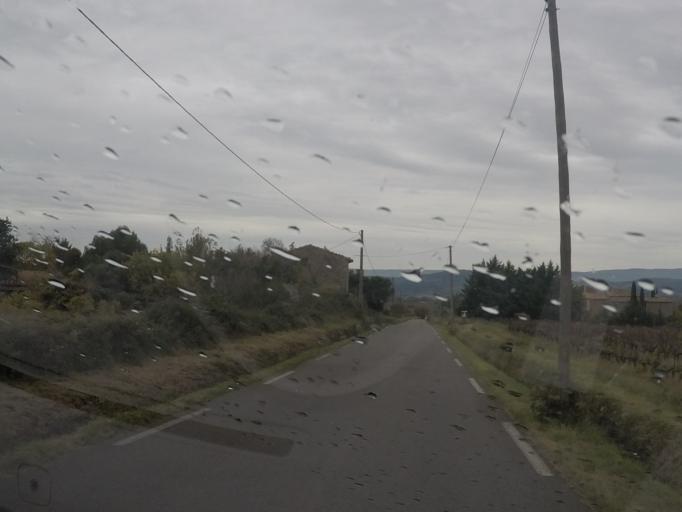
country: FR
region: Provence-Alpes-Cote d'Azur
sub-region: Departement du Vaucluse
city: Bonnieux
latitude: 43.8352
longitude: 5.2943
